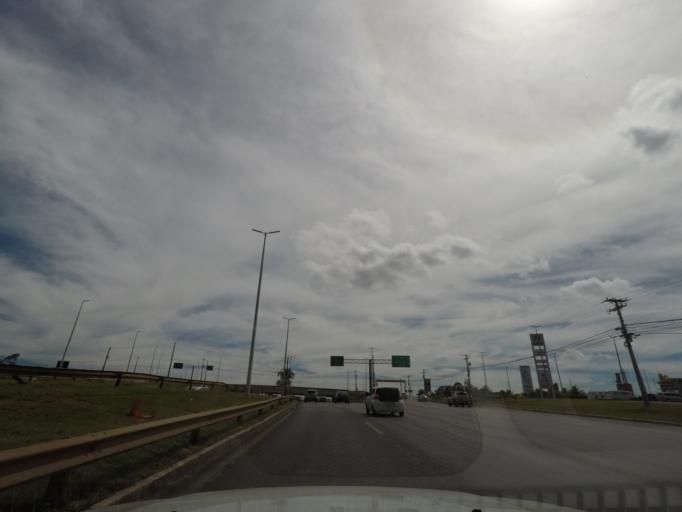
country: BR
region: Federal District
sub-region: Brasilia
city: Brasilia
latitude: -15.6898
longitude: -47.8621
